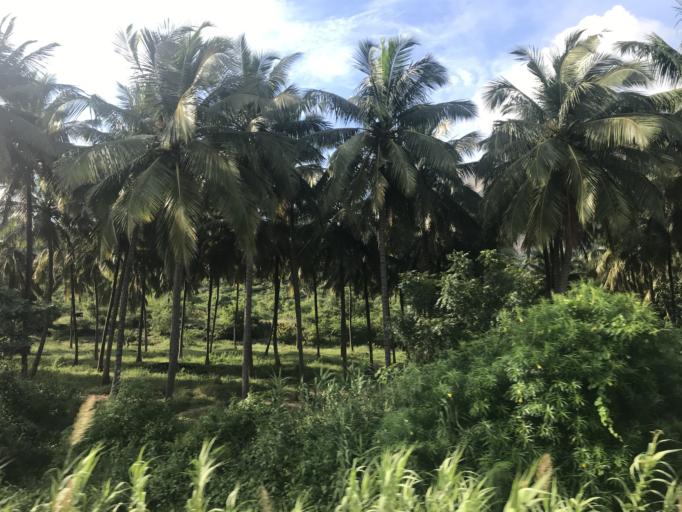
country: IN
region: Tamil Nadu
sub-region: Coimbatore
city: Madukkarai
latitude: 10.8945
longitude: 76.8842
